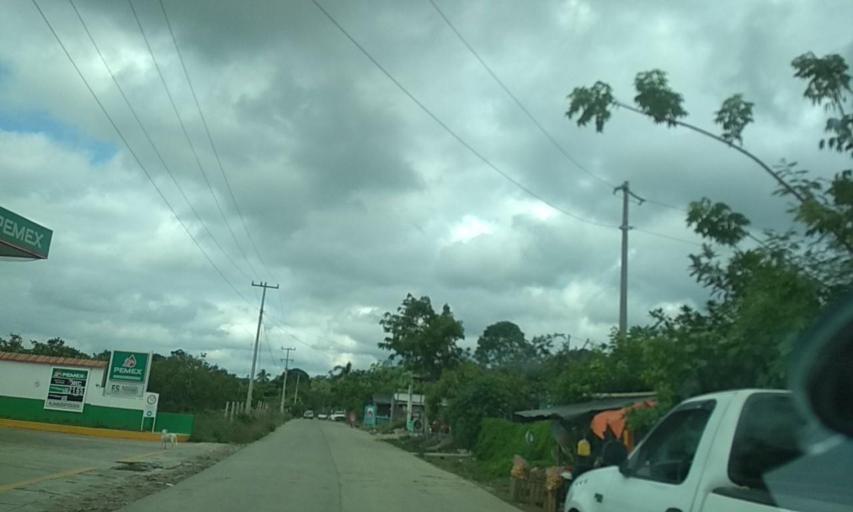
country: MX
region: Veracruz
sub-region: Papantla
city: Polutla
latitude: 20.5403
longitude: -97.2512
